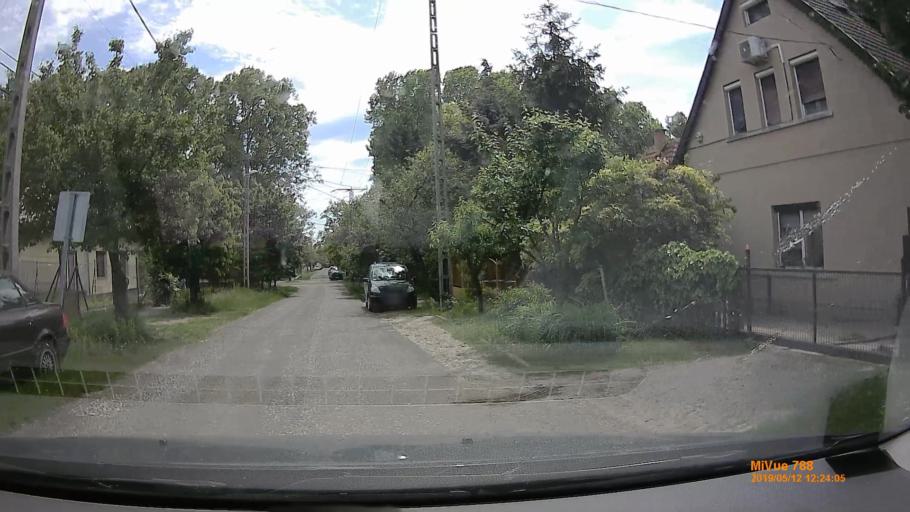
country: HU
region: Pest
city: Ecser
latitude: 47.4589
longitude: 19.2974
